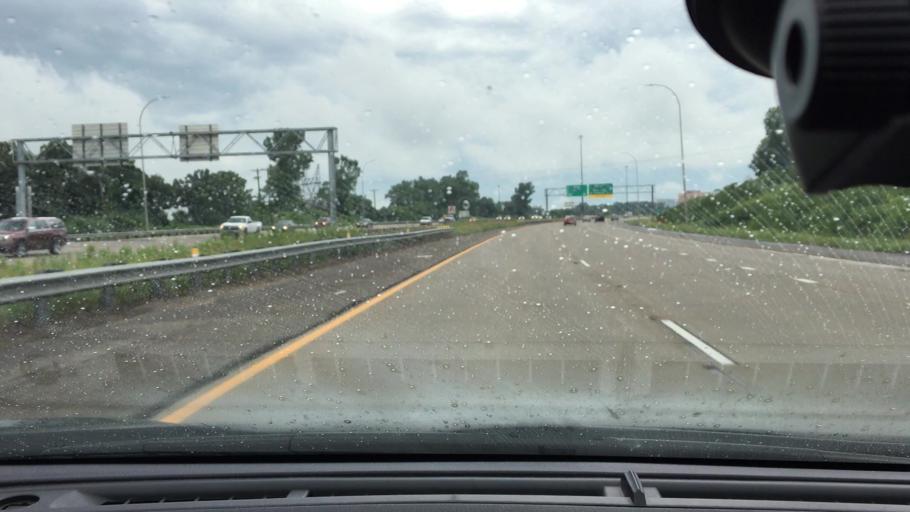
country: US
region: Minnesota
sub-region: Dakota County
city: Mendota Heights
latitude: 44.8668
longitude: -93.2023
